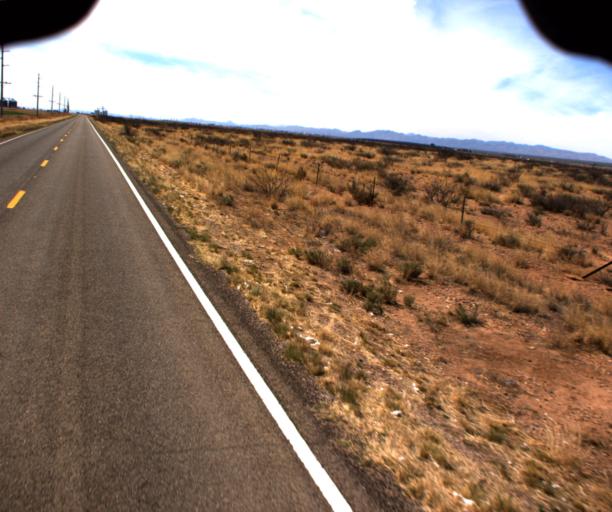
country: US
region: Arizona
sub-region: Cochise County
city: Tombstone
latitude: 31.7795
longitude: -109.6913
